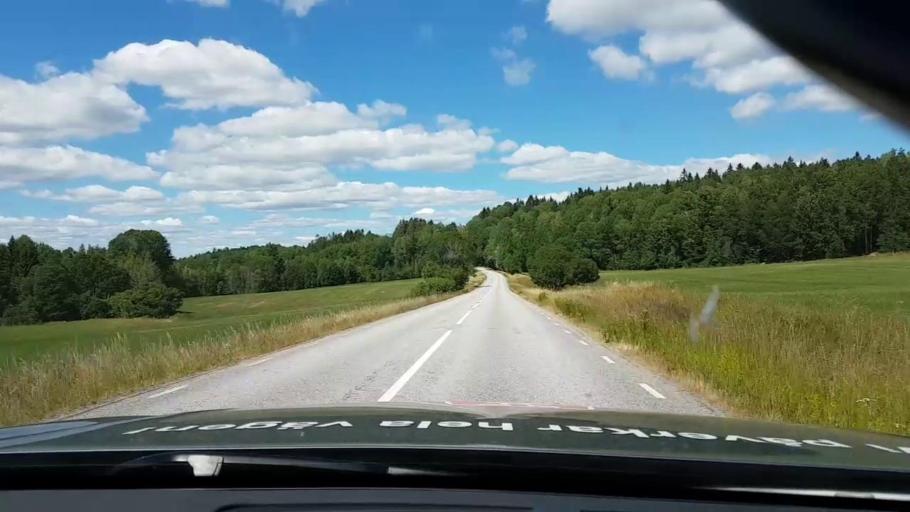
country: SE
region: Kalmar
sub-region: Vasterviks Kommun
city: Overum
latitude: 58.0617
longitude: 16.4027
